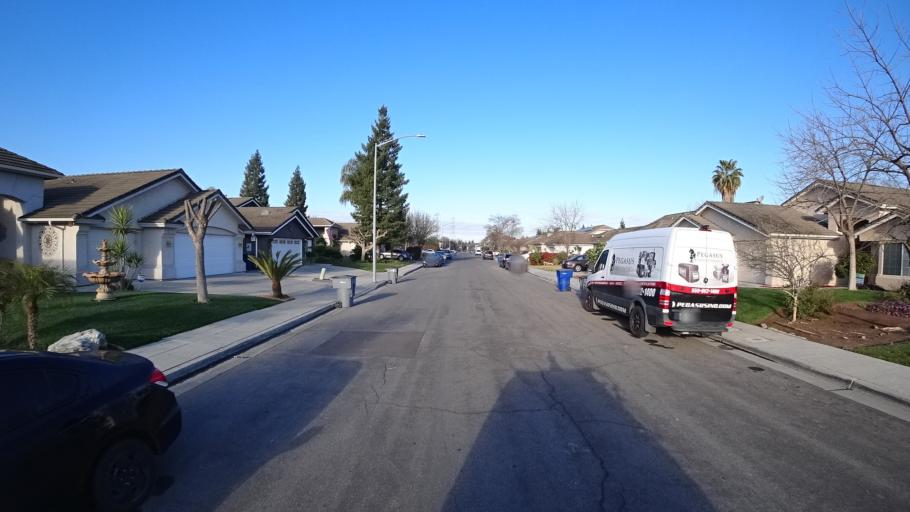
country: US
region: California
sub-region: Fresno County
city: West Park
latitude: 36.8194
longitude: -119.8743
